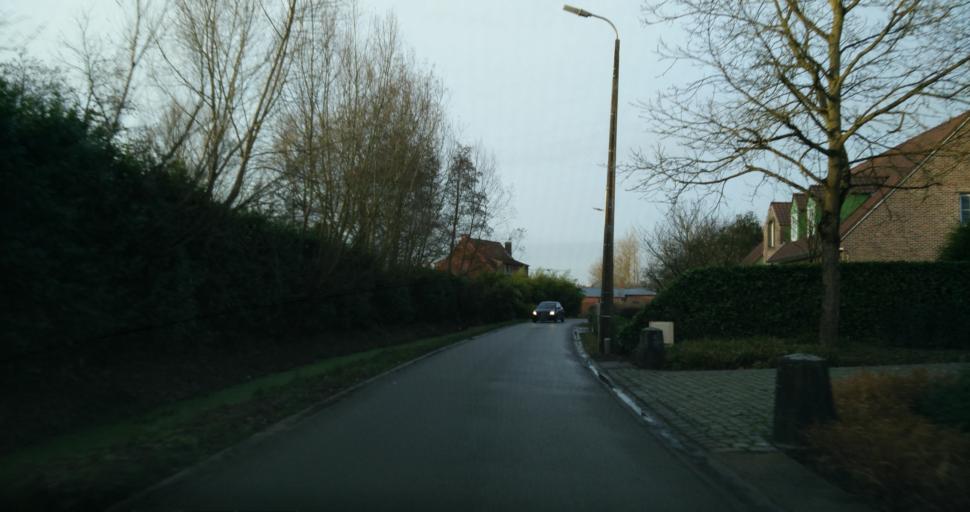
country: BE
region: Flanders
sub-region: Provincie Oost-Vlaanderen
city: Temse
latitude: 51.1086
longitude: 4.2194
